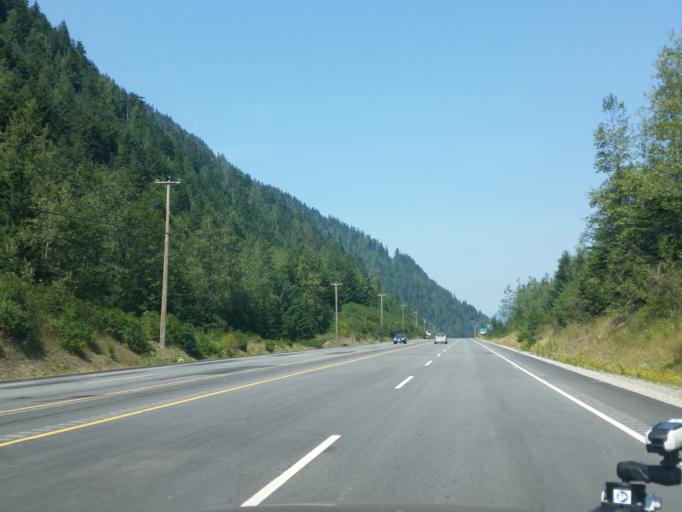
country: CA
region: British Columbia
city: Hope
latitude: 49.2944
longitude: -121.2604
